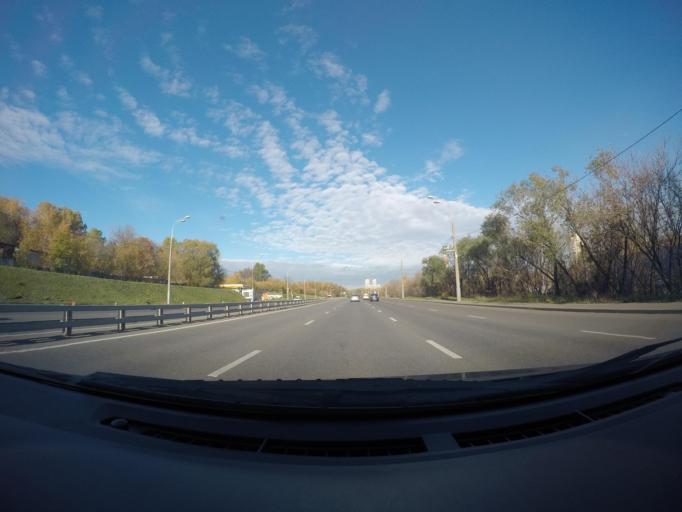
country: RU
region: Moscow
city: Sokol'niki
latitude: 55.8111
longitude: 37.6919
